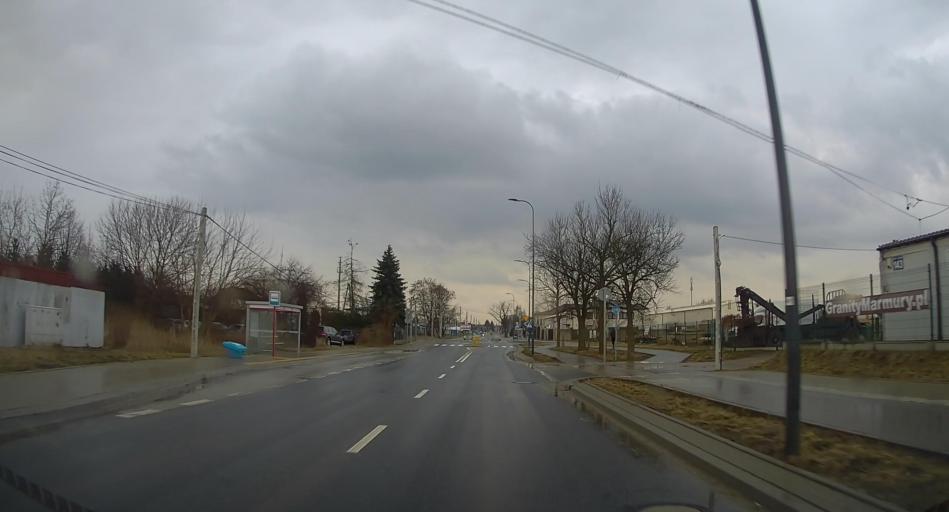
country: PL
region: Masovian Voivodeship
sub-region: Warszawa
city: Wawer
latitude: 52.1944
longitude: 21.1377
